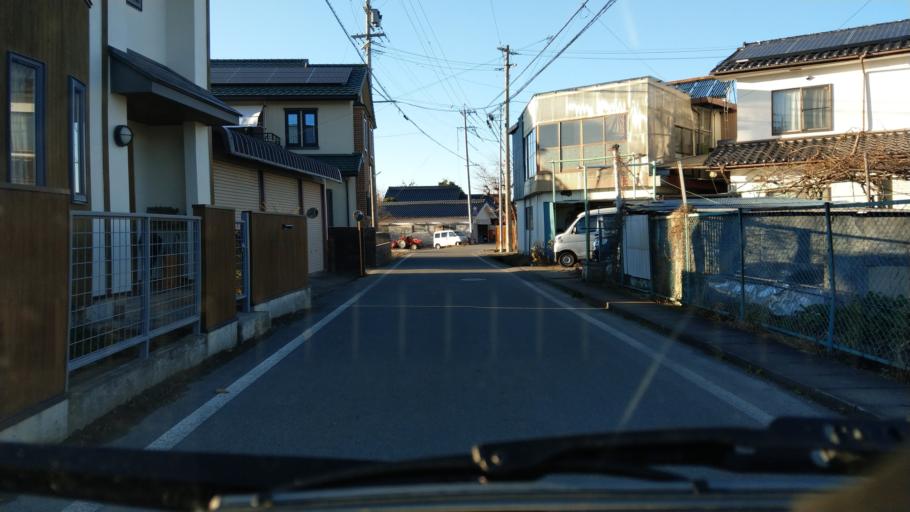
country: JP
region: Nagano
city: Saku
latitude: 36.2386
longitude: 138.4713
